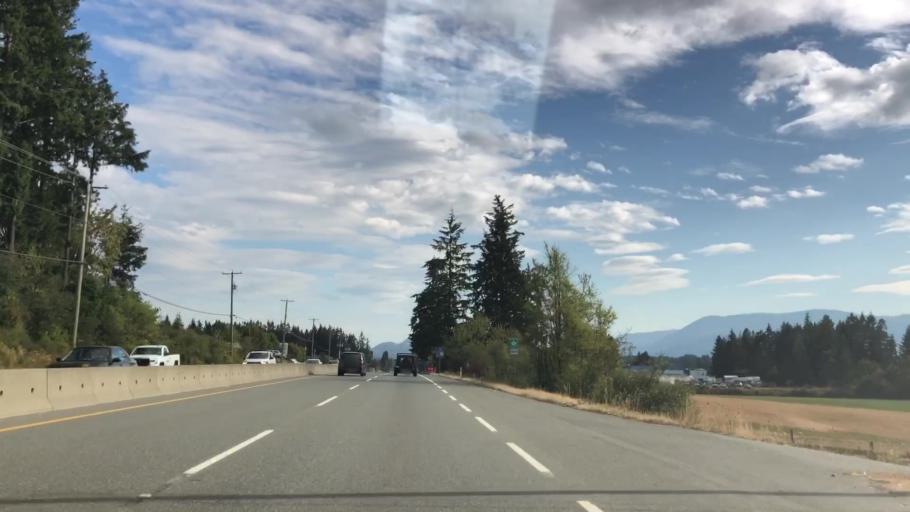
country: CA
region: British Columbia
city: Duncan
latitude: 48.8096
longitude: -123.7175
